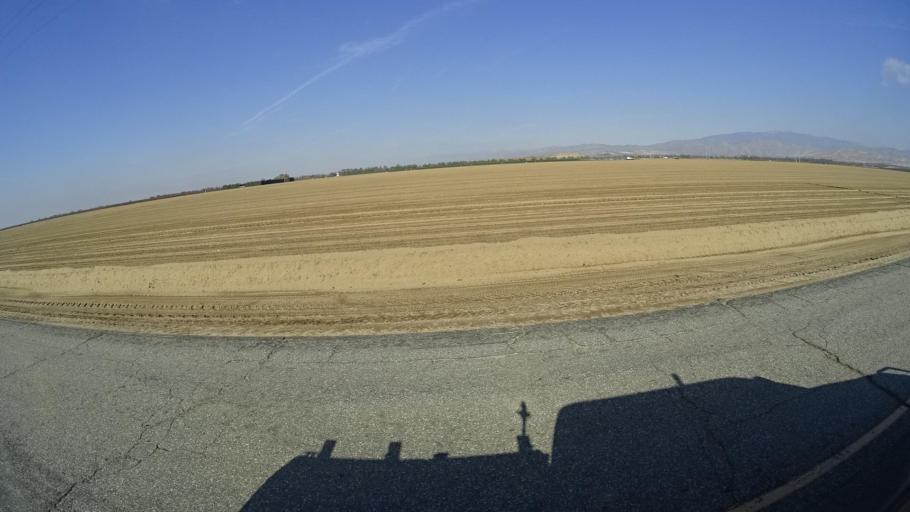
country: US
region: California
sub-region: Kern County
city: Arvin
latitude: 35.2675
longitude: -118.8120
